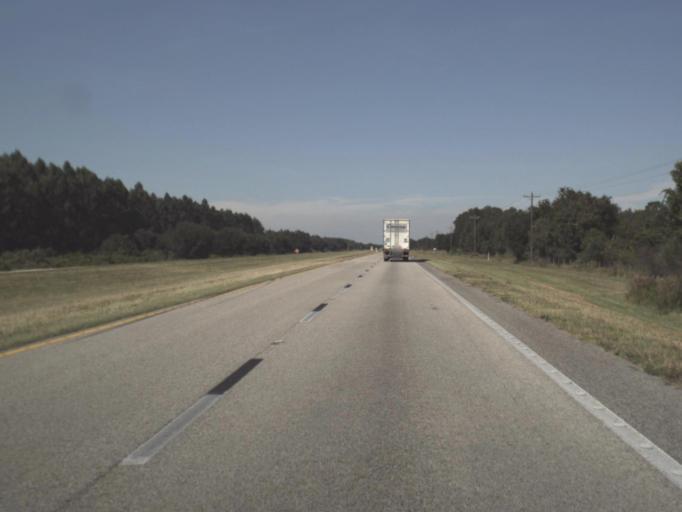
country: US
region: Florida
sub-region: Hendry County
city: Port LaBelle
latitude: 26.9952
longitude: -81.3272
